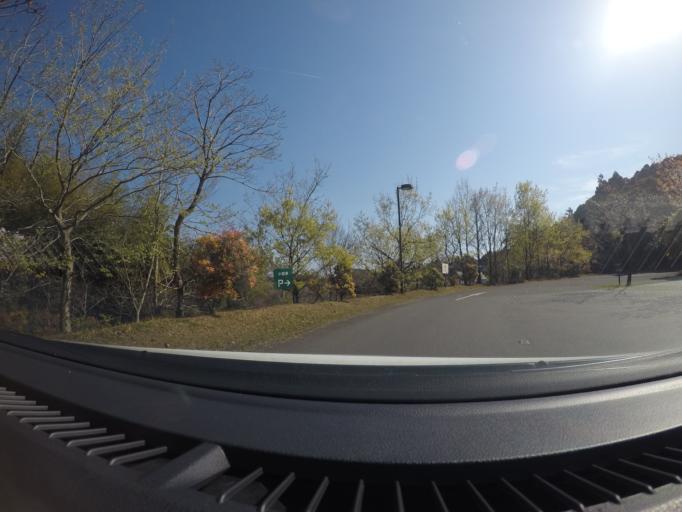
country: JP
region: Kochi
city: Kochi-shi
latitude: 33.5479
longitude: 133.5780
